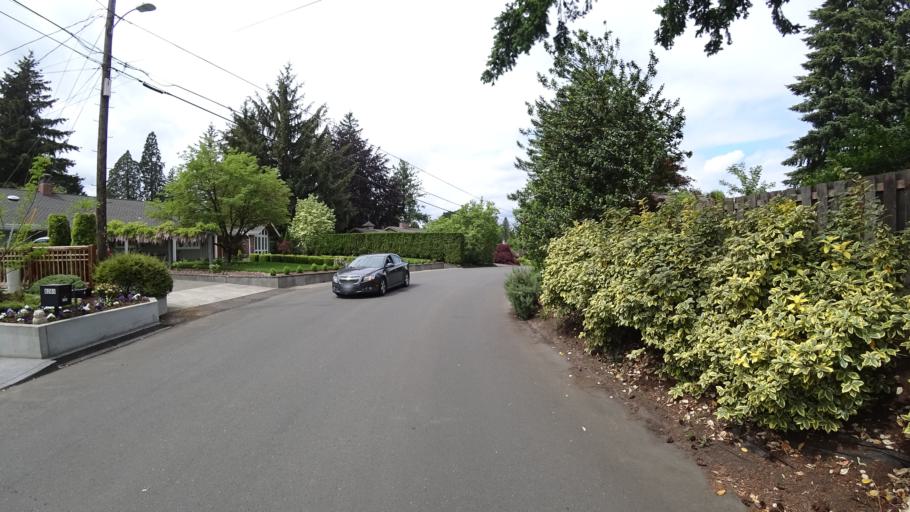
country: US
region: Oregon
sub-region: Washington County
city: Raleigh Hills
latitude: 45.4748
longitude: -122.7693
